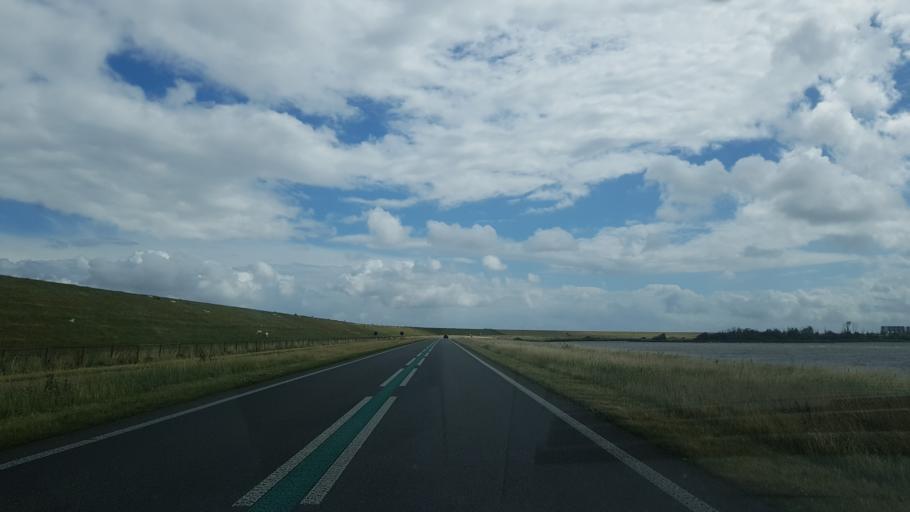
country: NL
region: Friesland
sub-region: Gemeente Dongeradeel
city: Anjum
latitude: 53.4123
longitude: 6.1711
